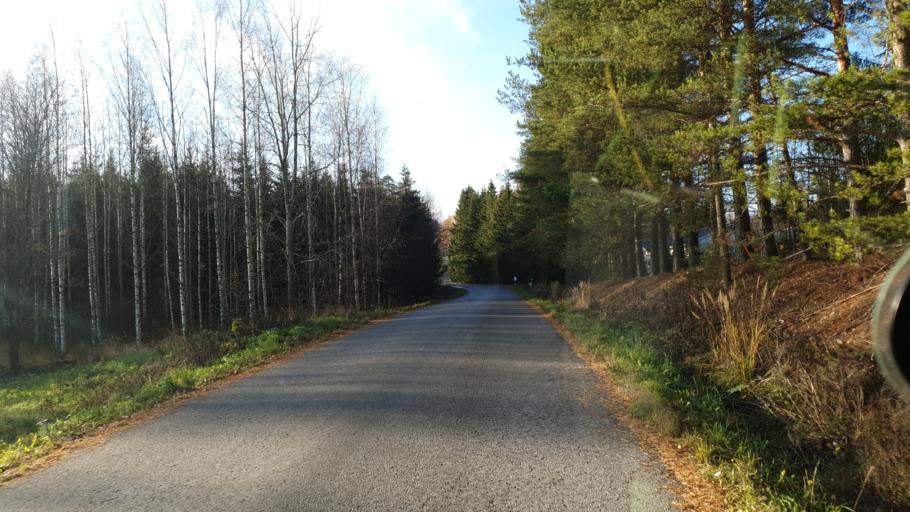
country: FI
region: Uusimaa
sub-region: Helsinki
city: Lohja
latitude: 60.2399
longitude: 24.1720
